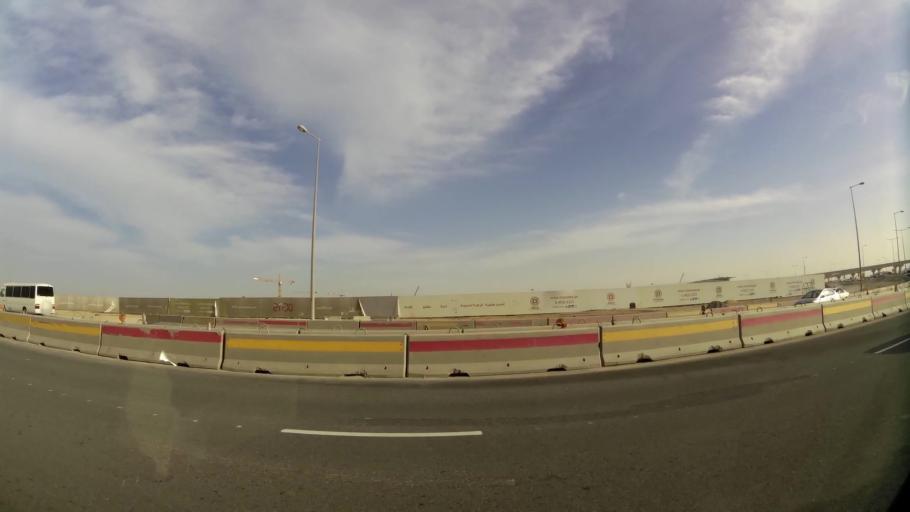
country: QA
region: Al Wakrah
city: Al Wakrah
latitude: 25.2183
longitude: 51.5864
